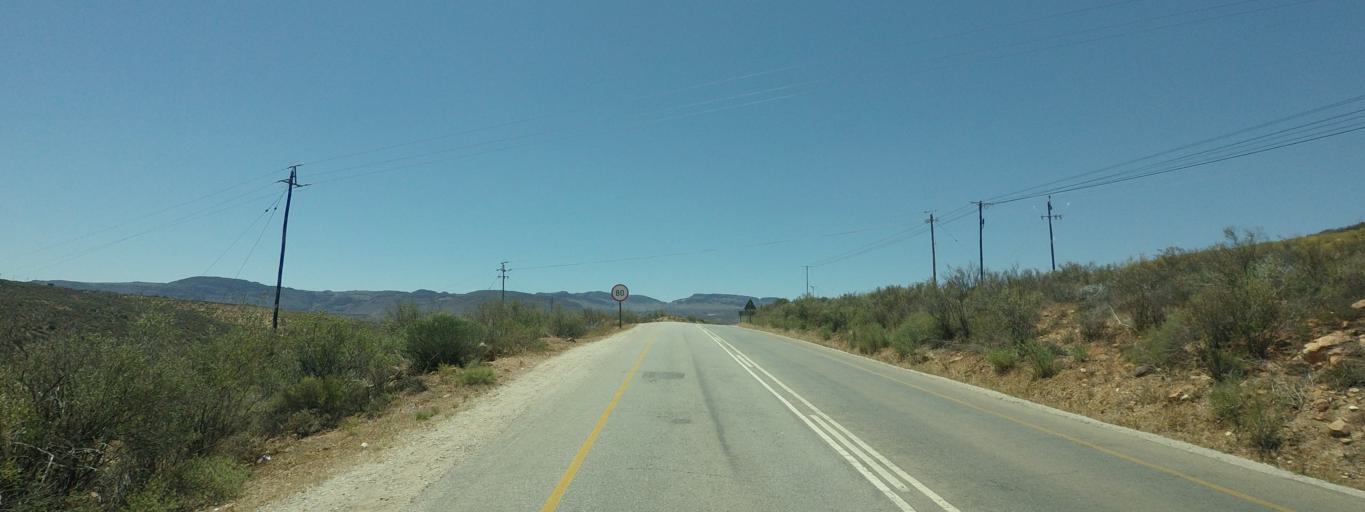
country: ZA
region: Western Cape
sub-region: West Coast District Municipality
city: Clanwilliam
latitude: -32.1715
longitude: 18.8729
